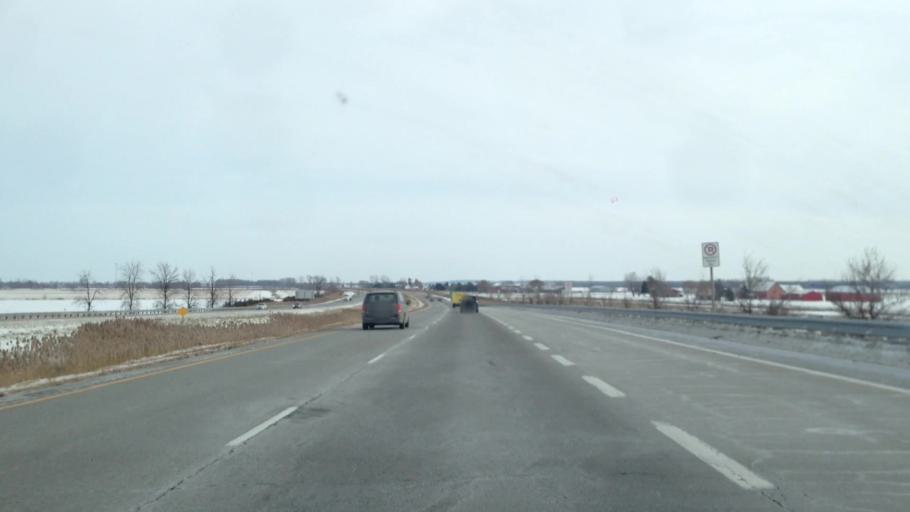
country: CA
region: Ontario
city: Casselman
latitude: 45.3041
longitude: -75.0666
